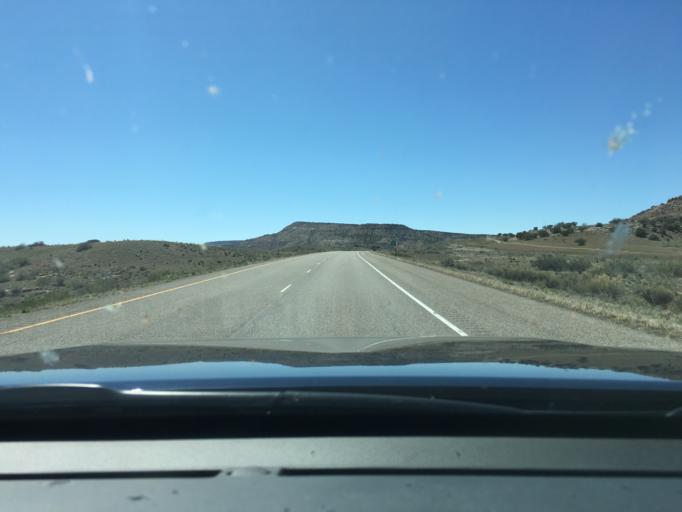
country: US
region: Colorado
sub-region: Mesa County
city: Loma
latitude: 39.1952
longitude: -109.0023
